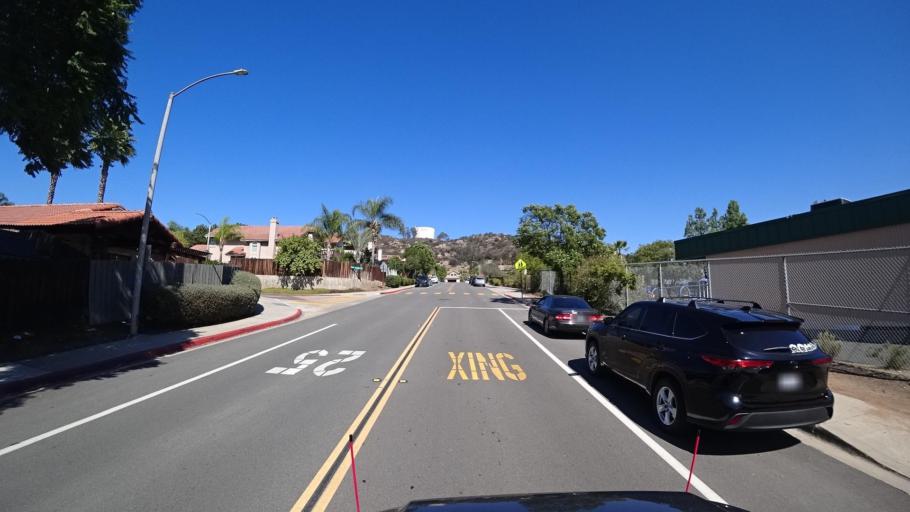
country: US
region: California
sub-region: San Diego County
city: Rancho San Diego
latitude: 32.7541
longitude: -116.9345
